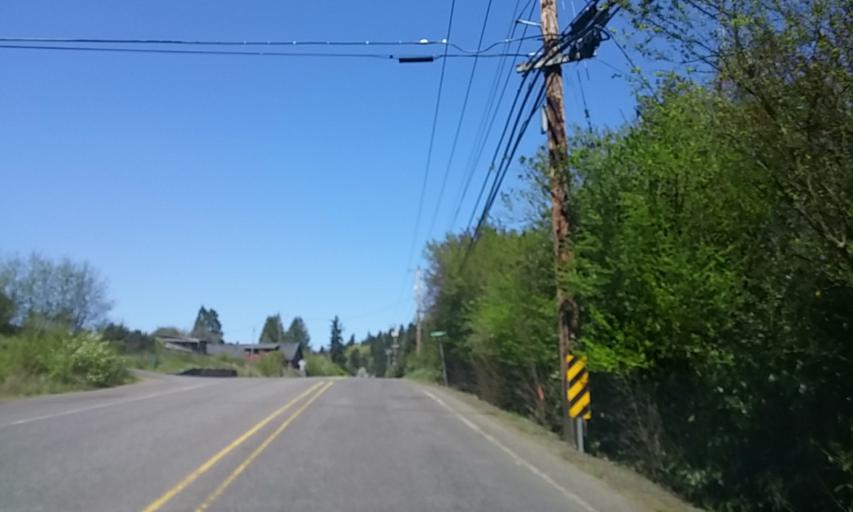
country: US
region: Oregon
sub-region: Washington County
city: West Haven-Sylvan
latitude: 45.5177
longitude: -122.7552
